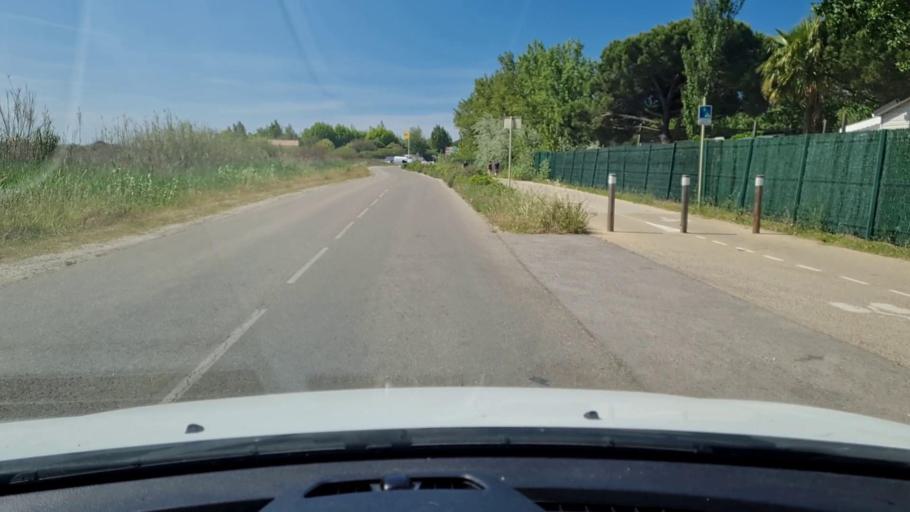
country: FR
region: Languedoc-Roussillon
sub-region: Departement du Gard
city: Le Grau-du-Roi
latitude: 43.5069
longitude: 4.1455
